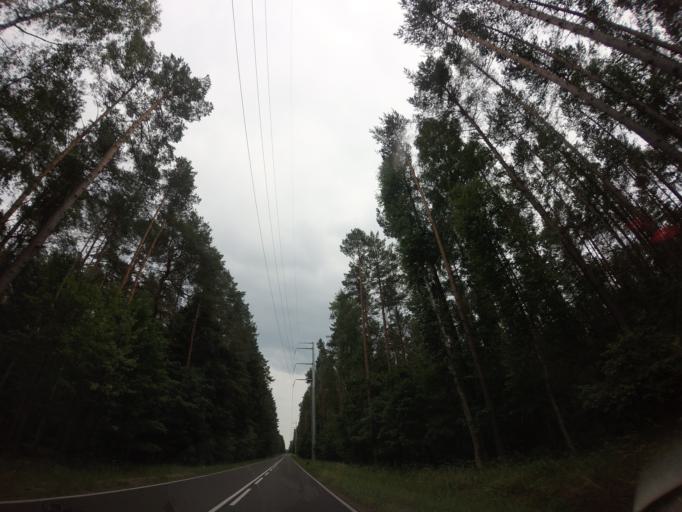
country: PL
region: West Pomeranian Voivodeship
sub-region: Powiat drawski
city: Czaplinek
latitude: 53.5005
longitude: 16.2222
